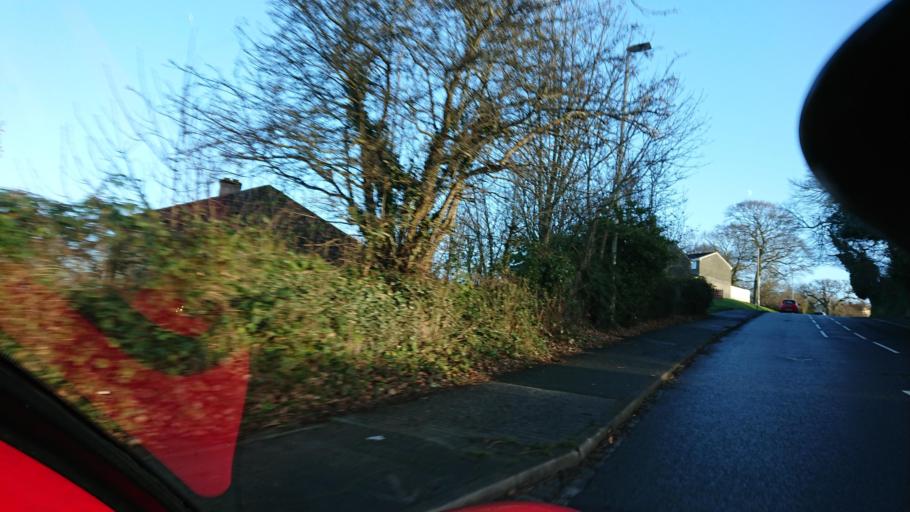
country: GB
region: England
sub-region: Plymouth
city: Plymouth
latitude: 50.4014
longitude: -4.1512
